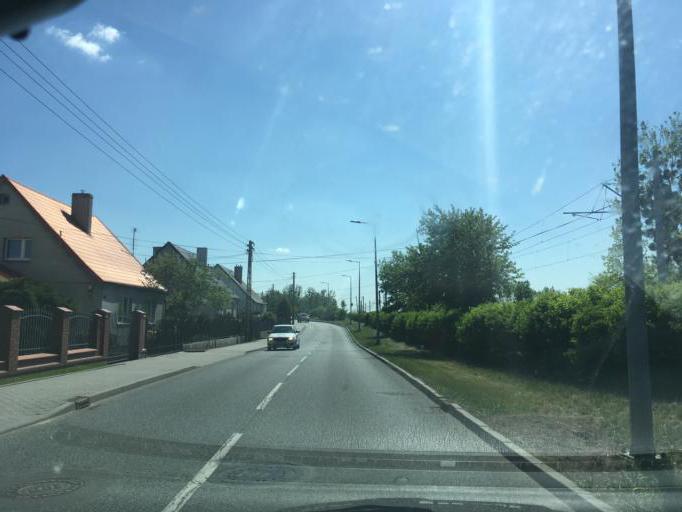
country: PL
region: Kujawsko-Pomorskie
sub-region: Bydgoszcz
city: Fordon
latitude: 53.1064
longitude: 18.1078
